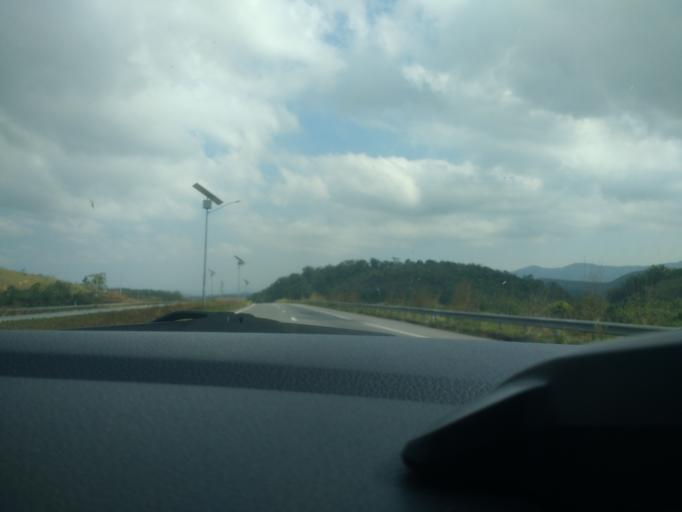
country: BR
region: Rio de Janeiro
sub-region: Queimados
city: Queimados
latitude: -22.6644
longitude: -43.5611
